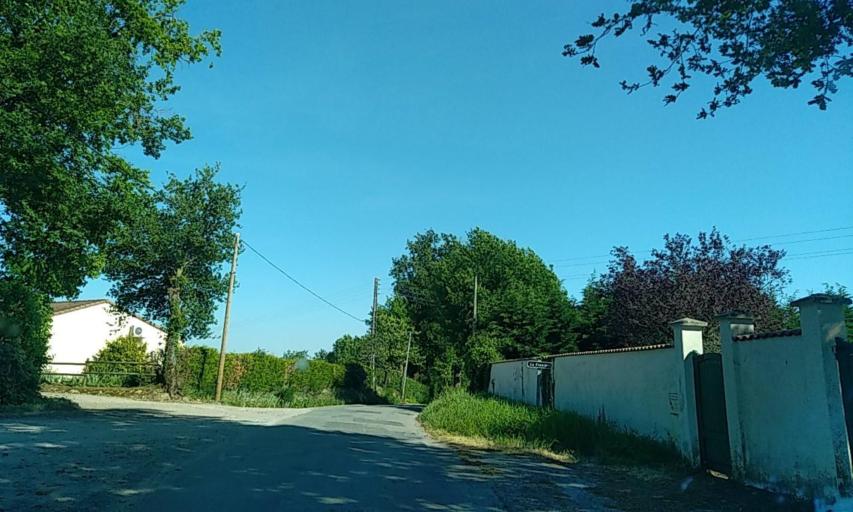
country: FR
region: Poitou-Charentes
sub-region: Departement des Deux-Sevres
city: Boisme
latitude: 46.7849
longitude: -0.4175
